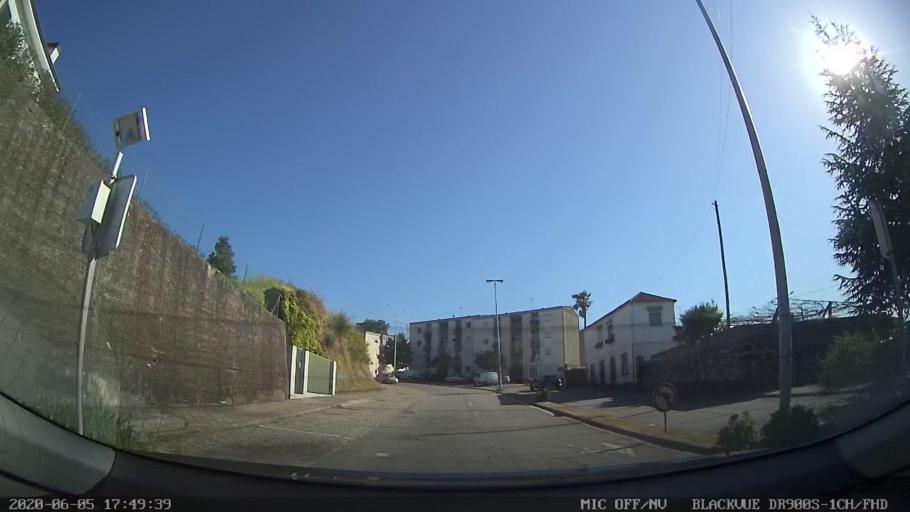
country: PT
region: Porto
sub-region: Penafiel
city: Penafiel
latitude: 41.2097
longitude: -8.2824
